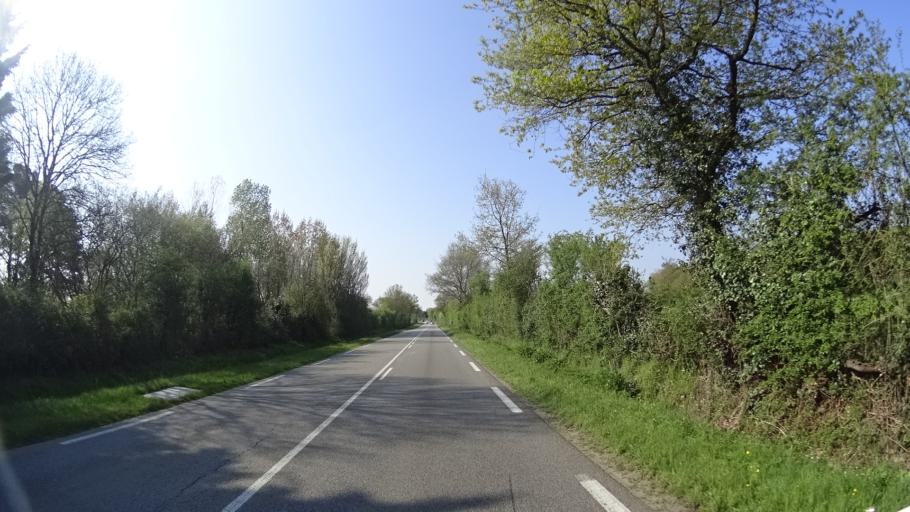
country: FR
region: Pays de la Loire
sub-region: Departement de la Loire-Atlantique
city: Port-Saint-Pere
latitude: 47.1262
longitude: -1.7624
